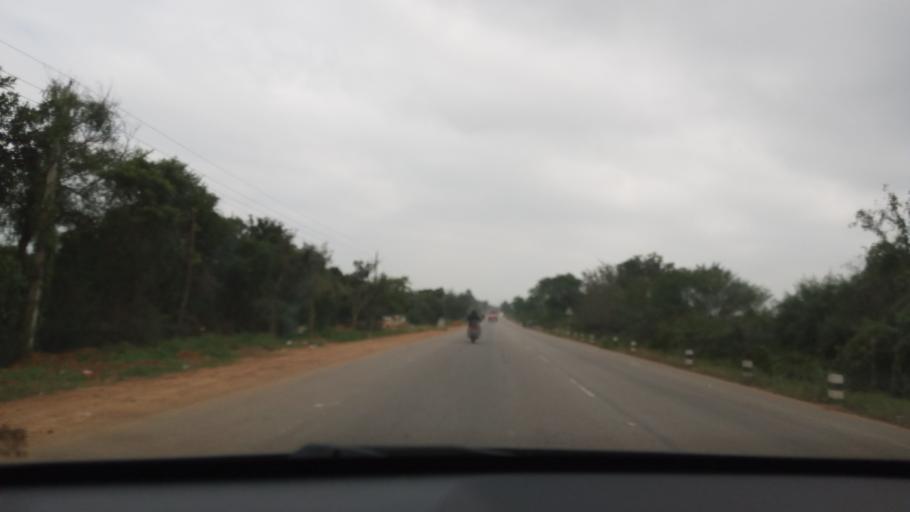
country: IN
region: Karnataka
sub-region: Bangalore Rural
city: Vijayapura
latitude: 13.2522
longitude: 77.9388
